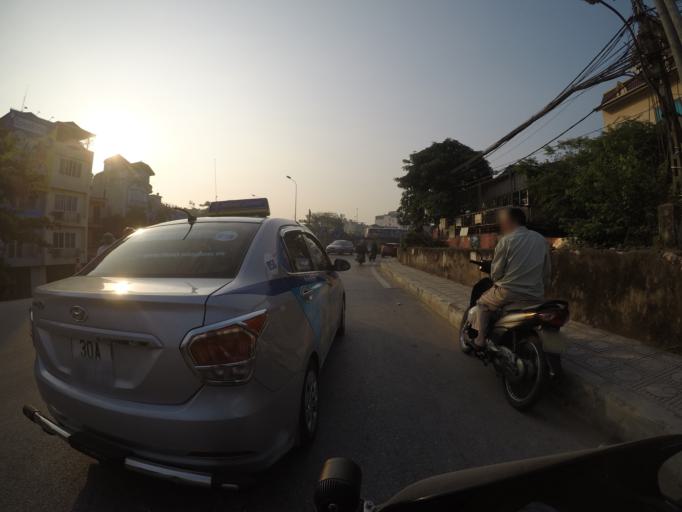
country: VN
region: Ha Noi
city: Hoan Kiem
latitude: 21.0405
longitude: 105.8654
